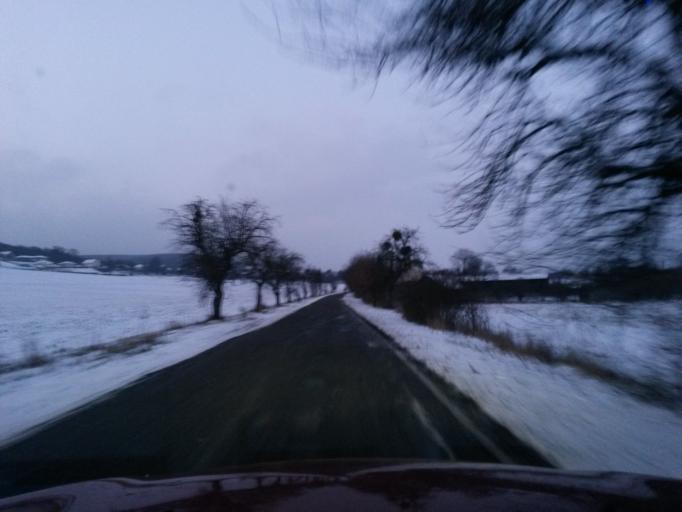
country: SK
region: Kosicky
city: Kosice
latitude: 48.7402
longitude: 21.3247
